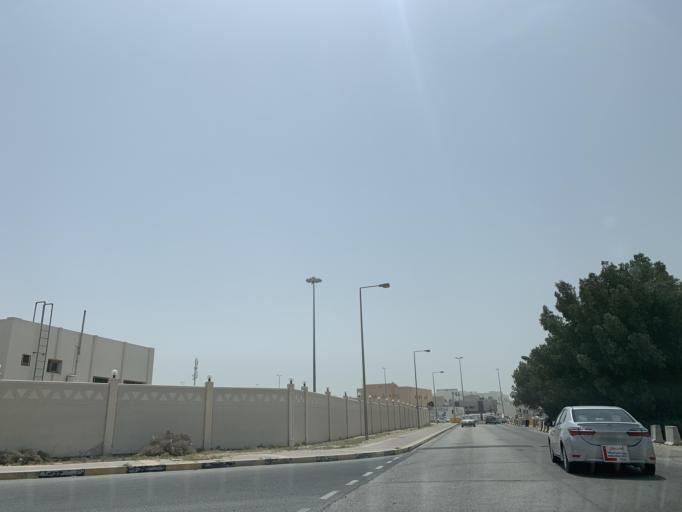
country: BH
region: Northern
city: Madinat `Isa
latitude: 26.1605
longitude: 50.5278
